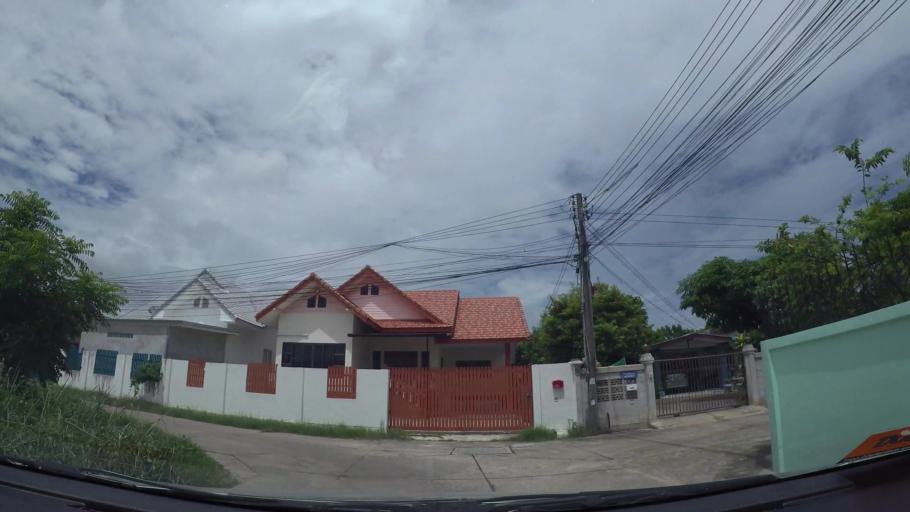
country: TH
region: Chon Buri
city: Sattahip
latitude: 12.6801
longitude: 100.8979
